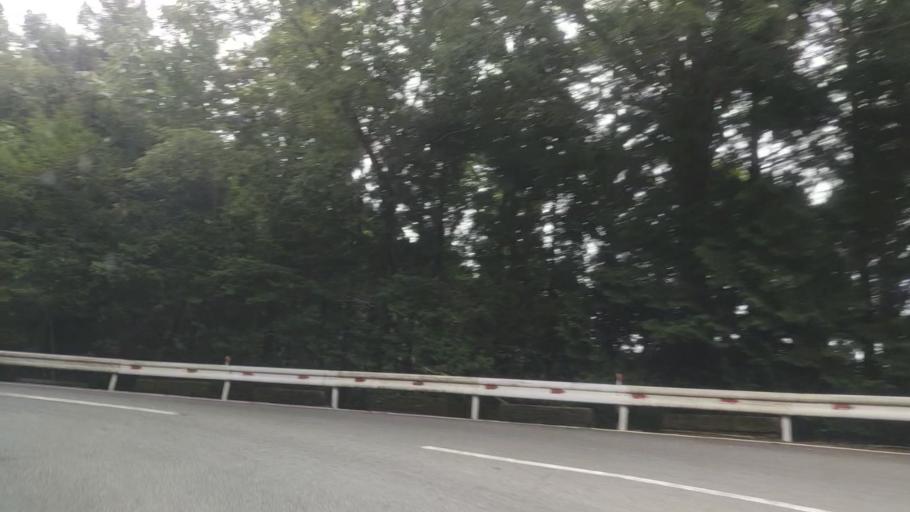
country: JP
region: Wakayama
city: Koya
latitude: 34.2095
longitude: 135.5436
